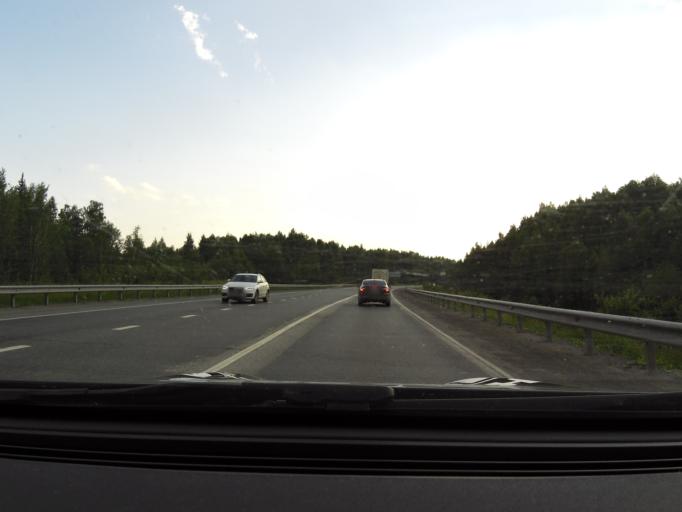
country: RU
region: Sverdlovsk
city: Talitsa
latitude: 56.8277
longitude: 59.9911
